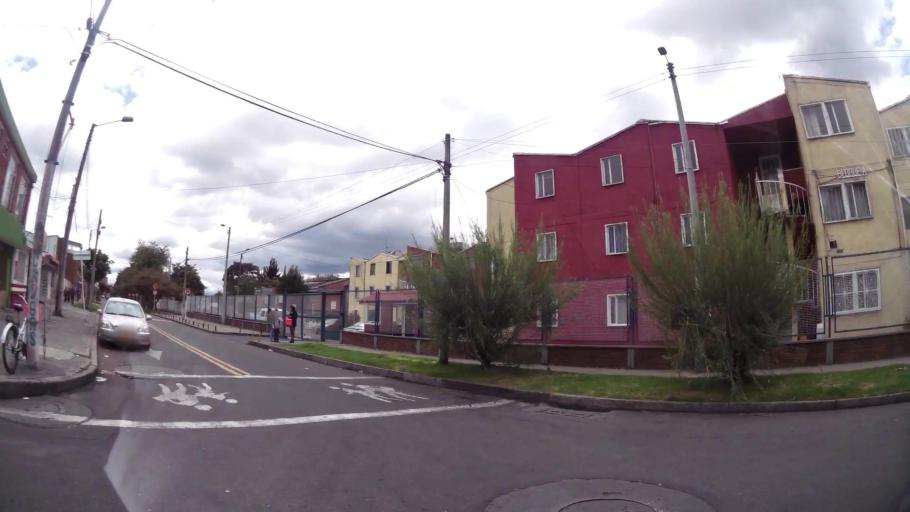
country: CO
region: Bogota D.C.
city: Barrio San Luis
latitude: 4.7011
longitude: -74.0938
